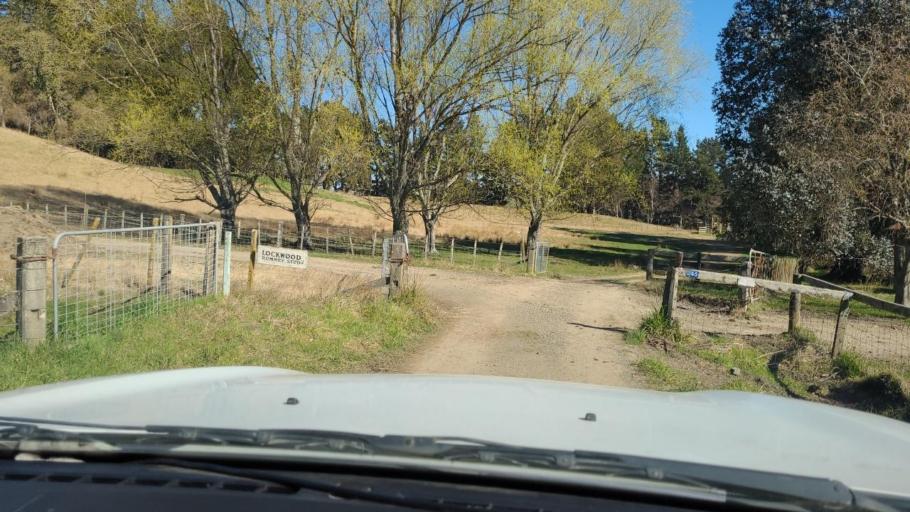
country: NZ
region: Hawke's Bay
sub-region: Napier City
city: Taradale
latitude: -39.4860
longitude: 176.4708
